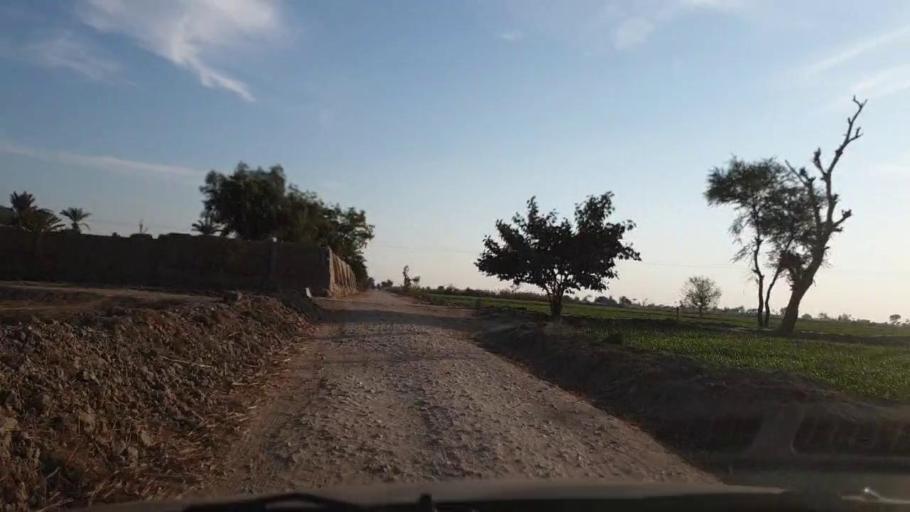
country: PK
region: Sindh
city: Khadro
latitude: 26.1715
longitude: 68.7530
